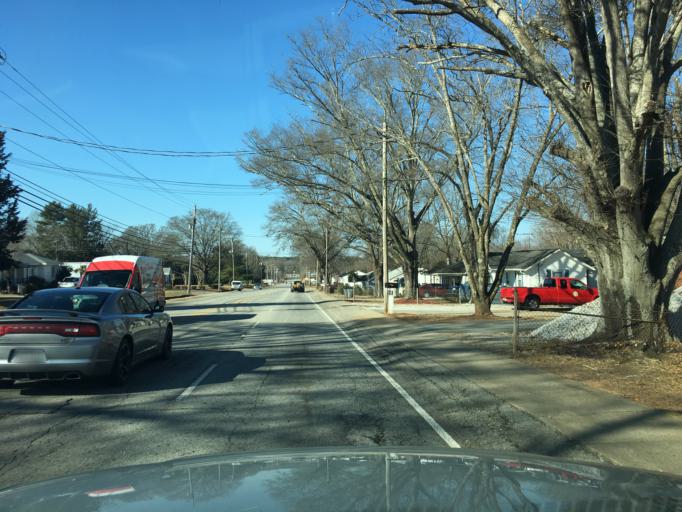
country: US
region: South Carolina
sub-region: Greenville County
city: Sans Souci
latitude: 34.8941
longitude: -82.4348
